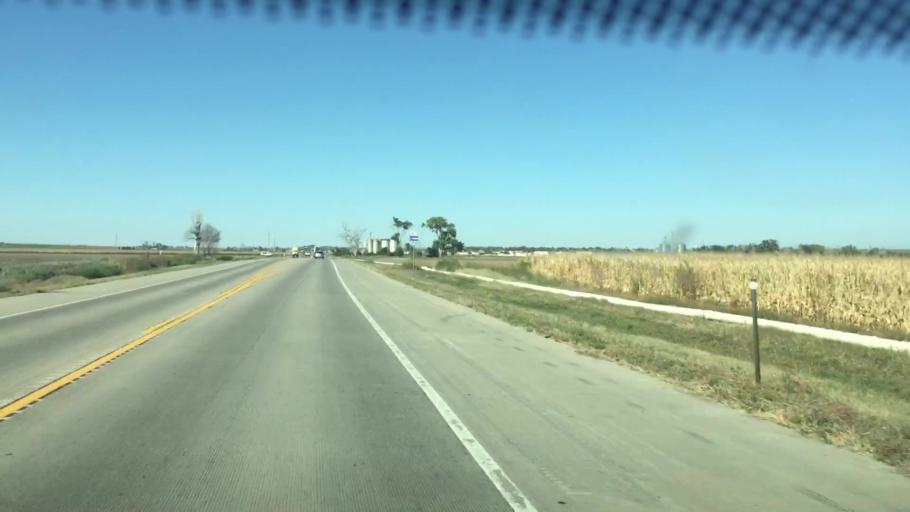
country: US
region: Colorado
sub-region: Prowers County
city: Lamar
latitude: 38.1392
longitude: -102.7237
